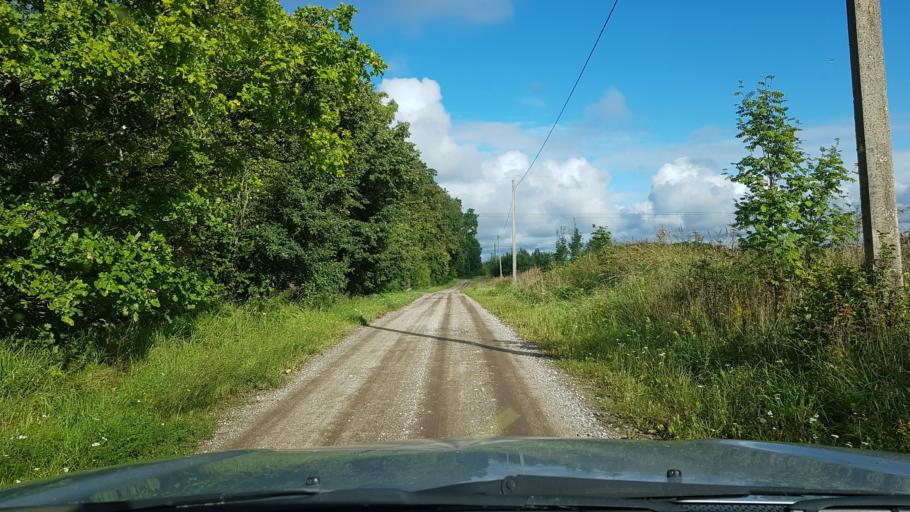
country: EE
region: Harju
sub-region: Rae vald
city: Vaida
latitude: 59.2688
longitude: 25.0272
